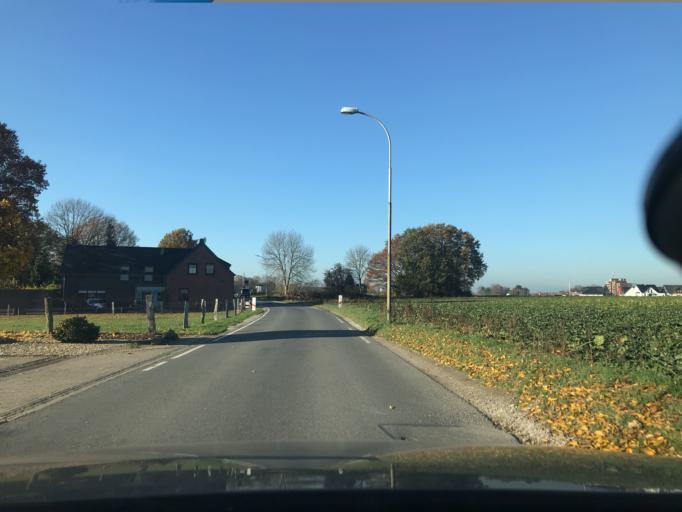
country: DE
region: North Rhine-Westphalia
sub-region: Regierungsbezirk Dusseldorf
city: Rheurdt
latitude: 51.4292
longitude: 6.4189
